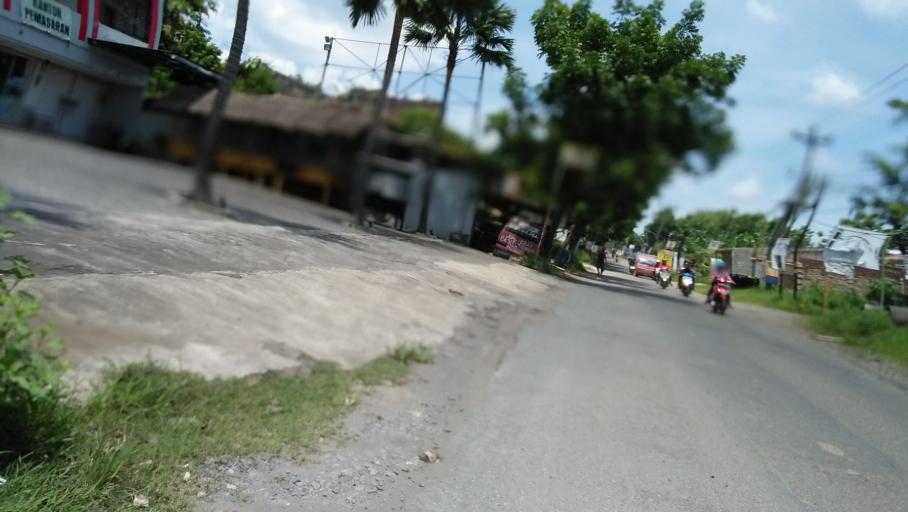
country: ID
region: Central Java
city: Mranggen
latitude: -7.0493
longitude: 110.4710
